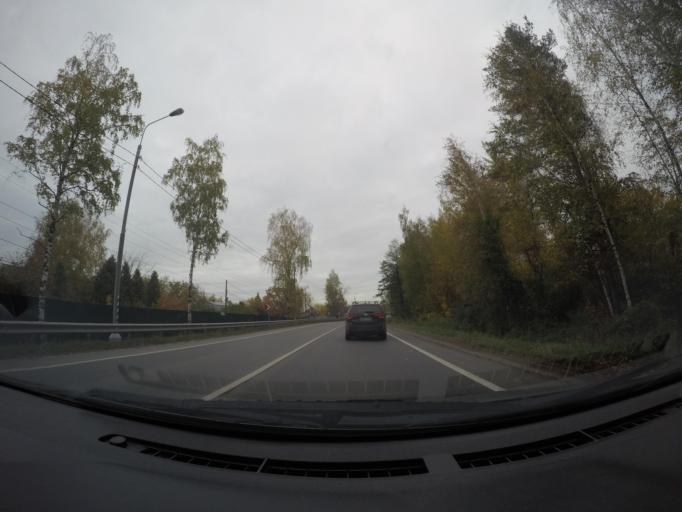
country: RU
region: Moskovskaya
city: Imeni Vorovskogo
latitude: 55.7281
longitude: 38.2912
